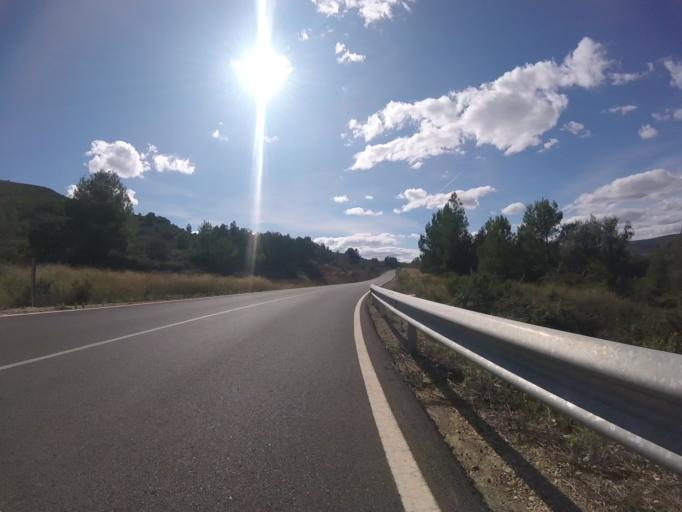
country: ES
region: Valencia
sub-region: Provincia de Castello
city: Cati
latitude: 40.4334
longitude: 0.0962
